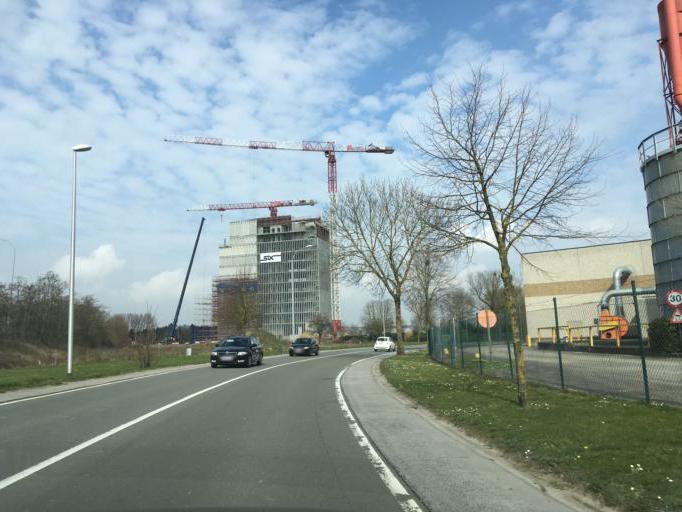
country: BE
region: Flanders
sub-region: Provincie West-Vlaanderen
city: Izegem
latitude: 50.9199
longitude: 3.1796
